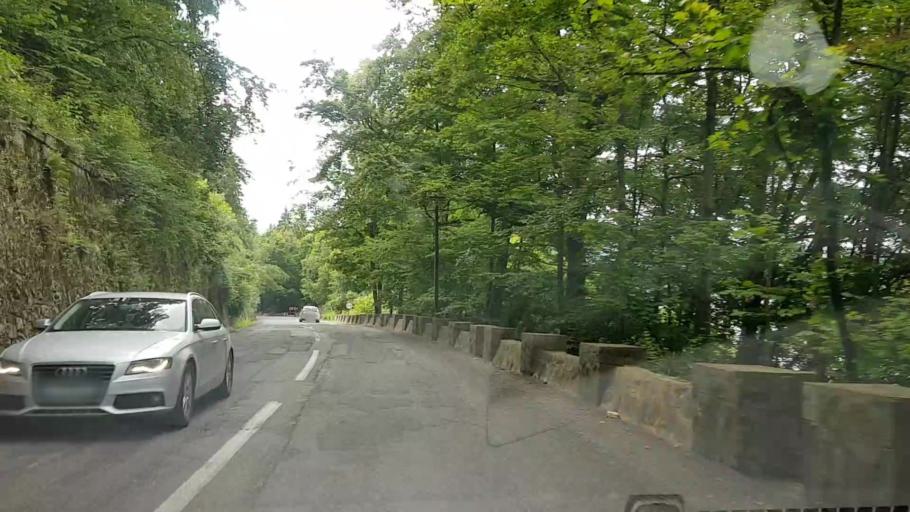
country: RO
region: Neamt
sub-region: Comuna Bicaz
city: Dodeni
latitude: 46.9385
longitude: 26.1173
